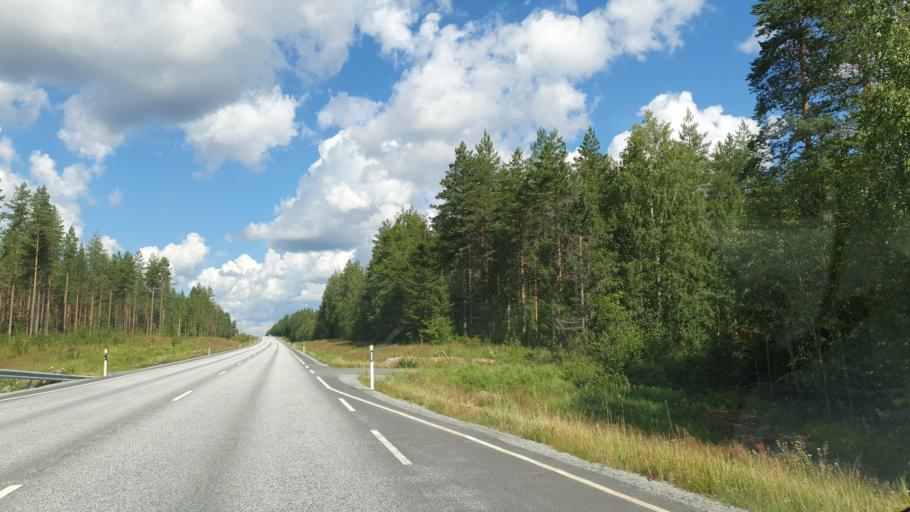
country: FI
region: Northern Savo
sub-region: Ylae-Savo
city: Sonkajaervi
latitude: 63.9518
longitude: 27.3744
